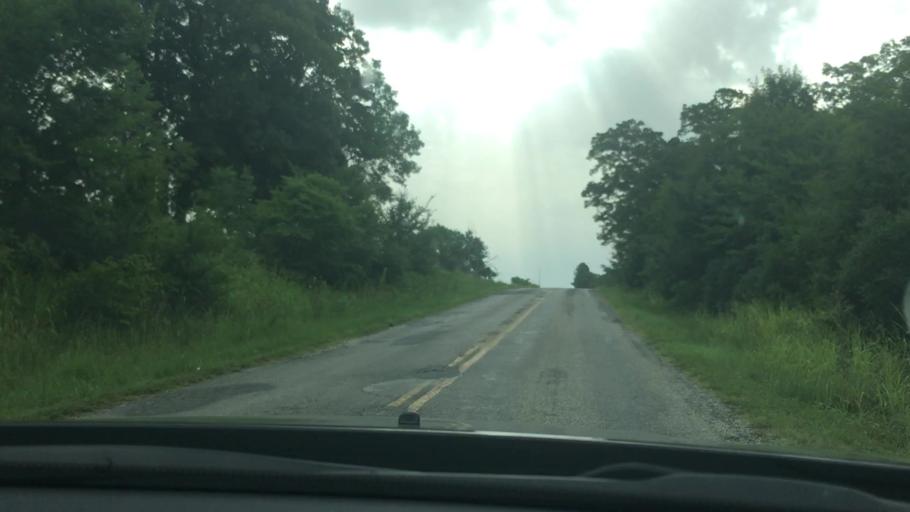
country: US
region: Oklahoma
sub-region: Pontotoc County
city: Ada
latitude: 34.8106
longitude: -96.6413
